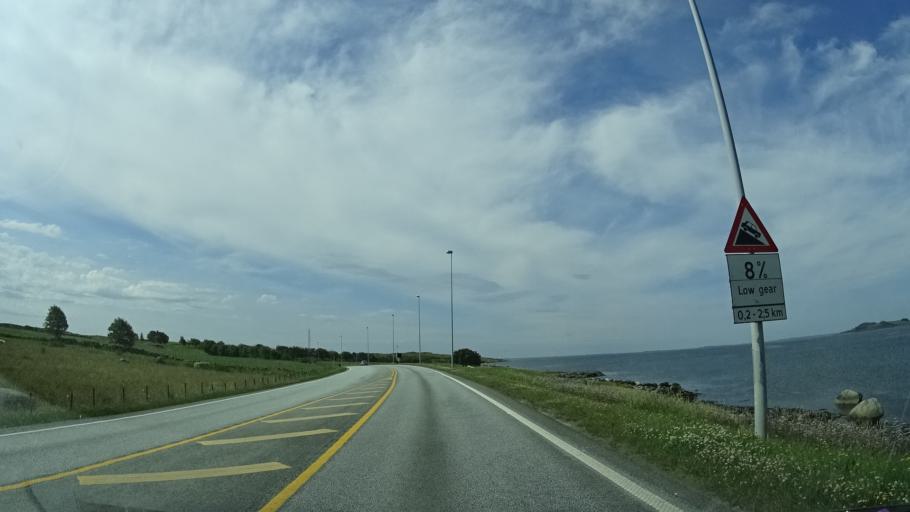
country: NO
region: Rogaland
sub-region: Rennesoy
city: Vikevag
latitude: 59.0564
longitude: 5.6618
